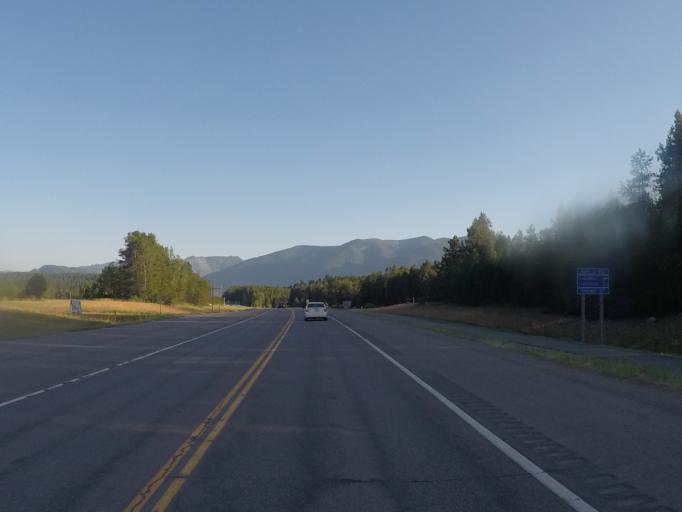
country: US
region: Montana
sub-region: Flathead County
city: Columbia Falls
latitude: 48.4368
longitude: -114.0420
